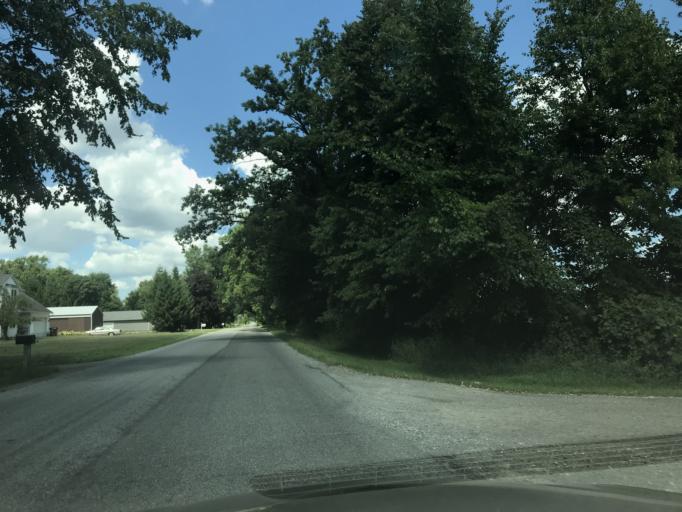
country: US
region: Michigan
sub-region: Ingham County
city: Holt
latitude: 42.6220
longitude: -84.5626
